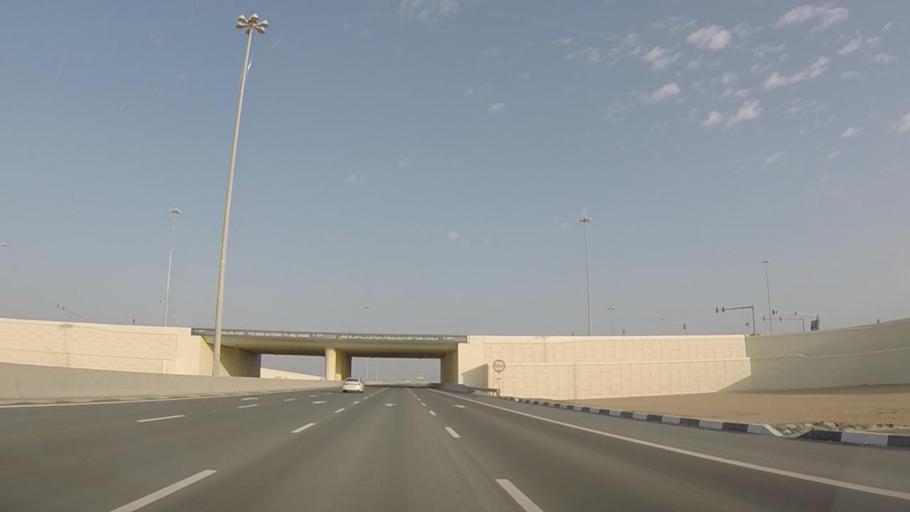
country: AE
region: Abu Dhabi
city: Abu Dhabi
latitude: 24.7350
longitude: 54.7419
